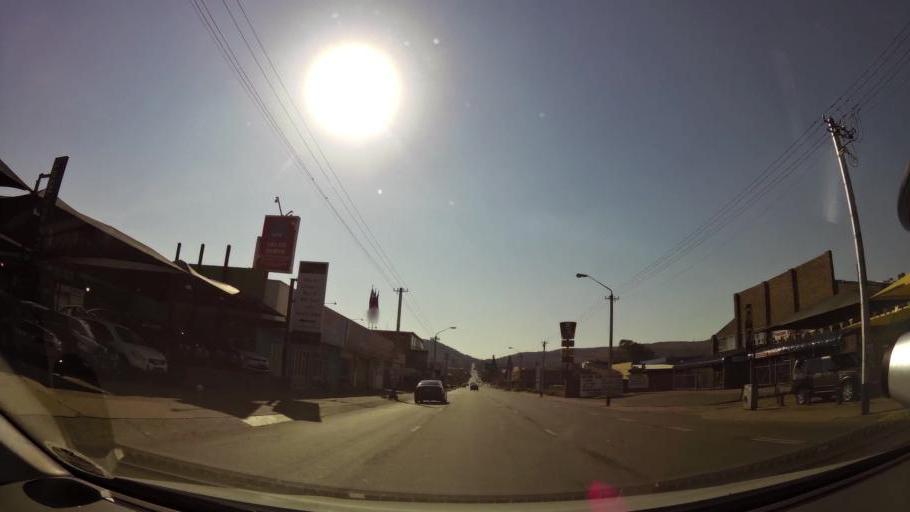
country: ZA
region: Gauteng
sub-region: City of Tshwane Metropolitan Municipality
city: Pretoria
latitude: -25.7086
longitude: 28.2009
